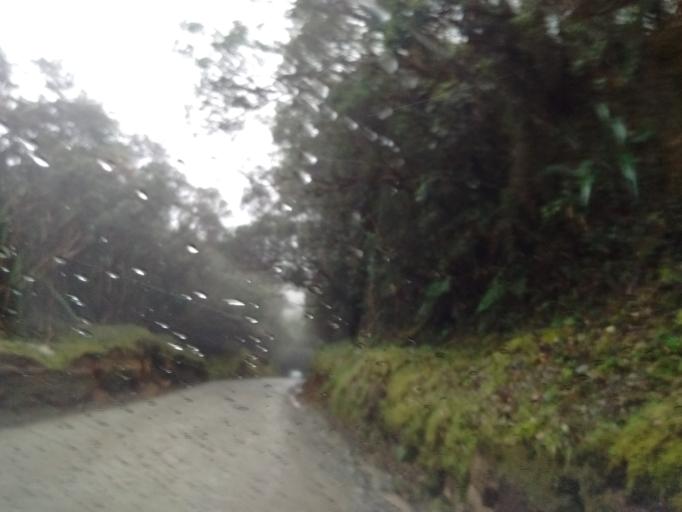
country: CO
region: Cauca
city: Paispamba
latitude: 2.1666
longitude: -76.4180
